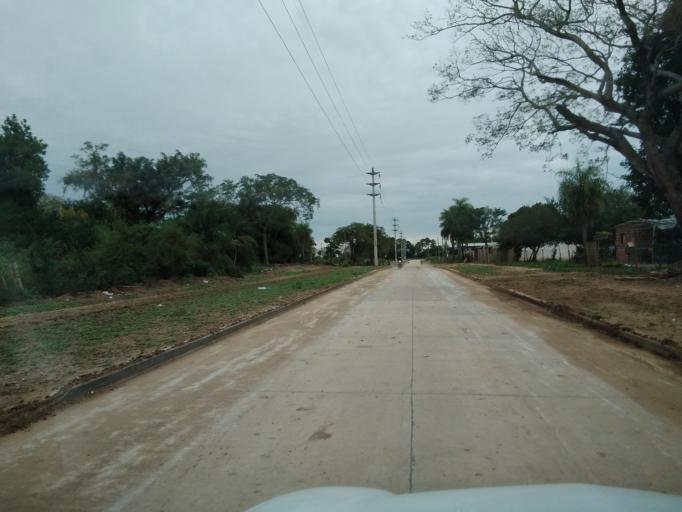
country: AR
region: Corrientes
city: Corrientes
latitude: -27.5144
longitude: -58.8215
